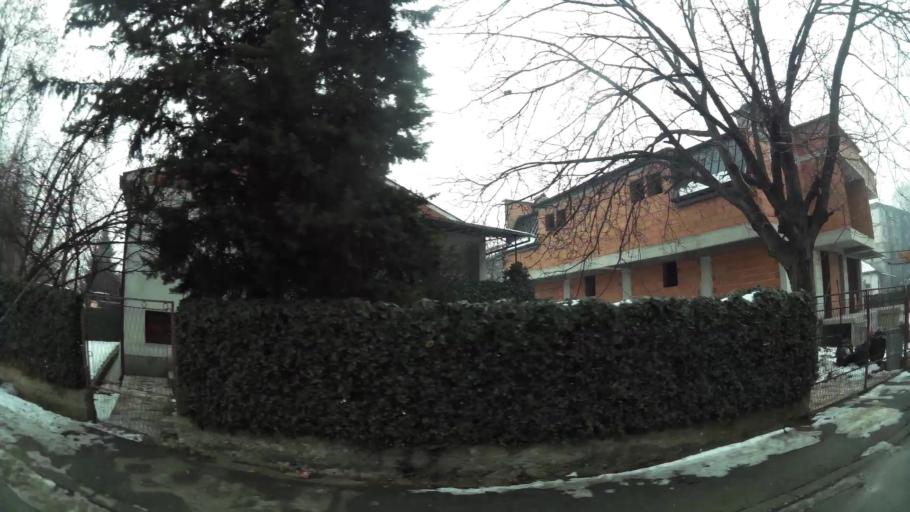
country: MK
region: Kisela Voda
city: Kisela Voda
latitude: 41.9985
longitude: 21.4955
